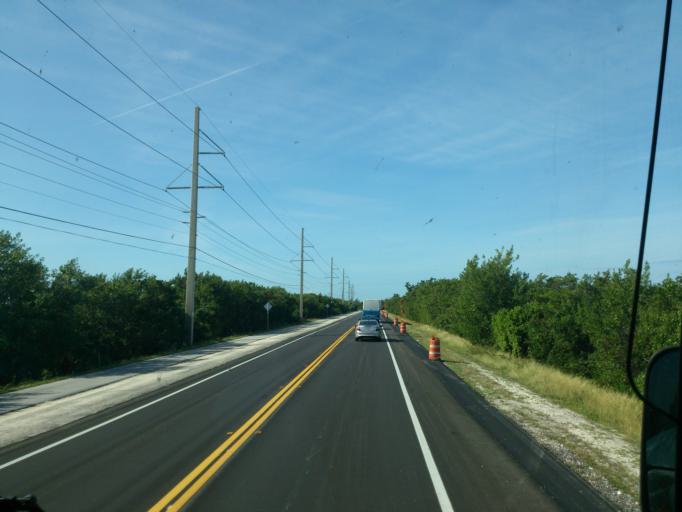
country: US
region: Florida
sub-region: Monroe County
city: Islamorada
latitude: 24.8394
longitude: -80.7932
